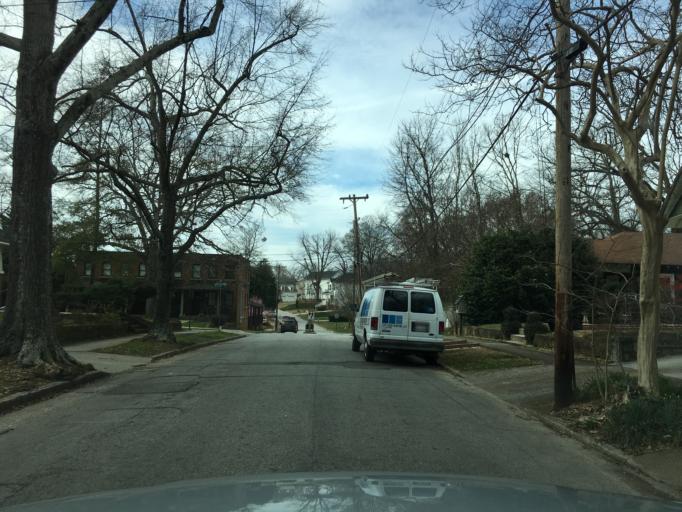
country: US
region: South Carolina
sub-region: Greenville County
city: Greenville
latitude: 34.8606
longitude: -82.3978
